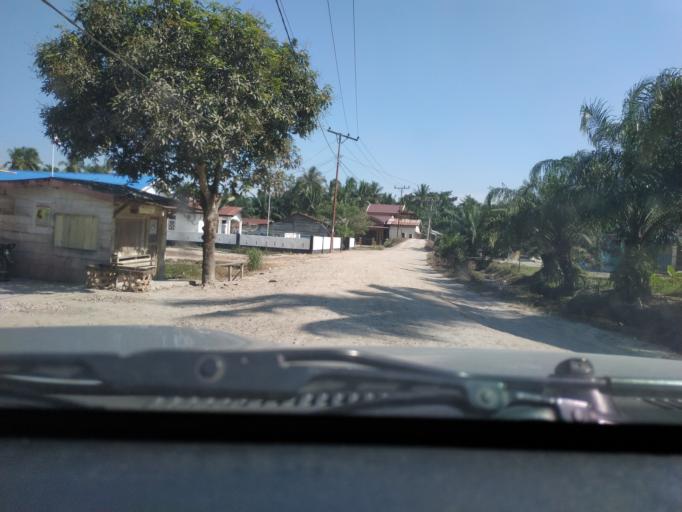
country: ID
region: North Sumatra
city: Tanjungbalai
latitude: 2.8356
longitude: 99.9704
